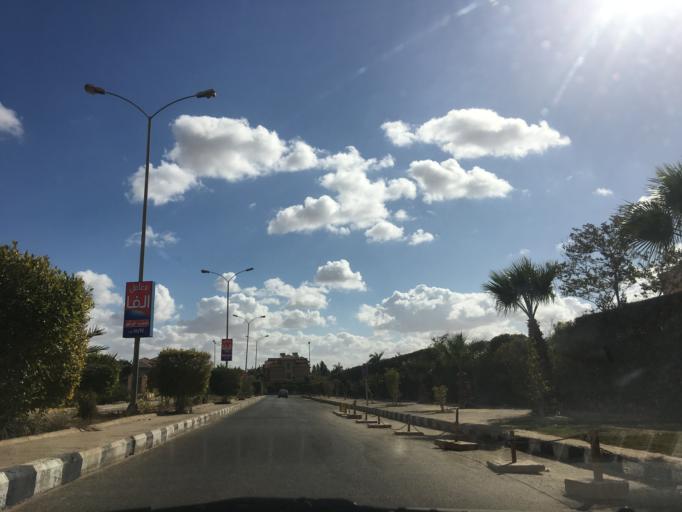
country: EG
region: Al Jizah
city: Madinat Sittah Uktubar
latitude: 29.9971
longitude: 30.9694
